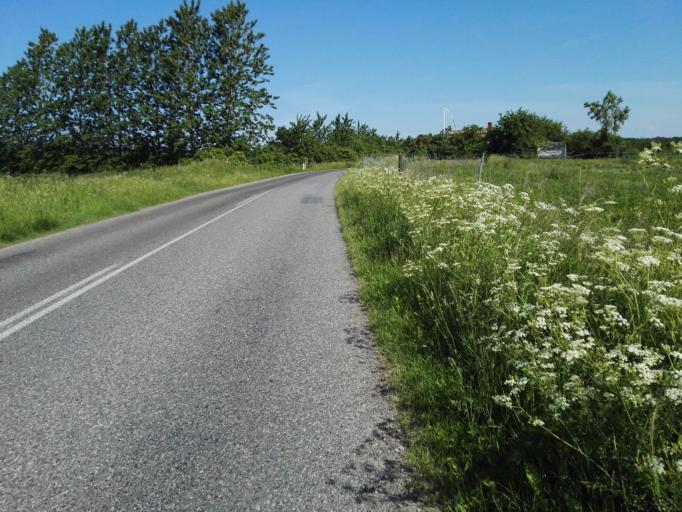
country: DK
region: Zealand
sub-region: Lejre Kommune
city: Ejby
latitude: 55.7216
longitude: 11.8886
